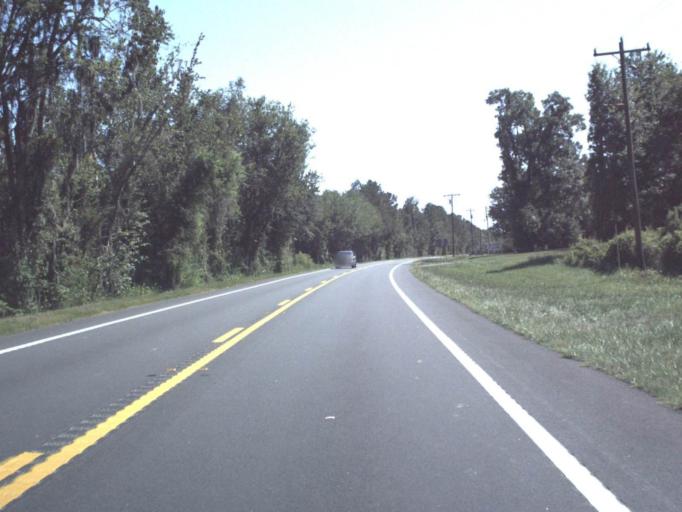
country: US
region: Florida
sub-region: Union County
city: Lake Butler
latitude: 29.9647
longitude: -82.4083
